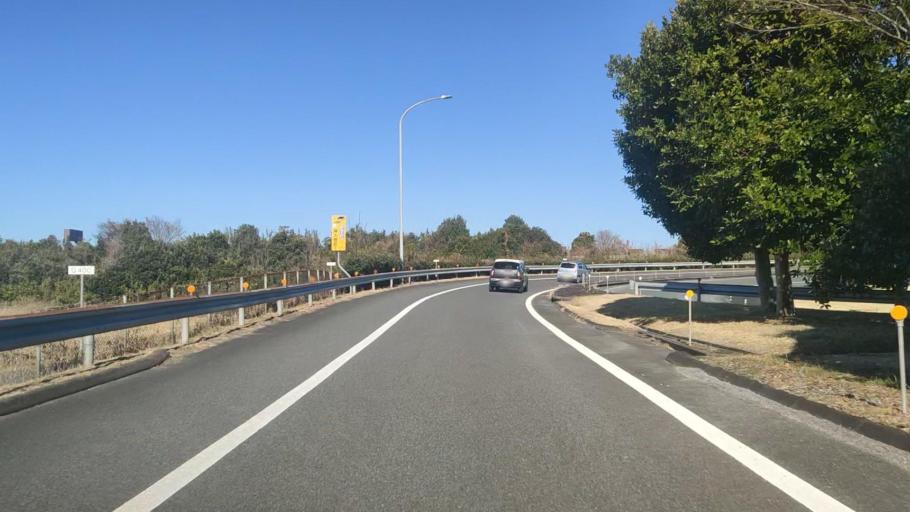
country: JP
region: Miyazaki
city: Miyakonojo
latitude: 31.7816
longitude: 131.1099
